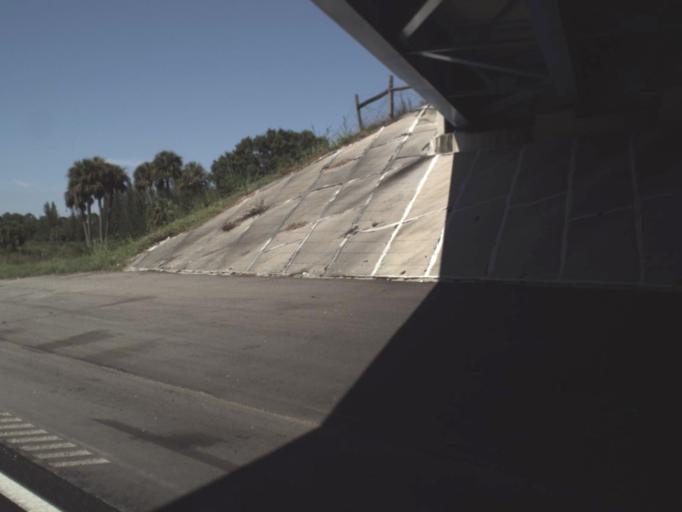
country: US
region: Florida
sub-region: Lee County
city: Suncoast Estates
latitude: 26.7399
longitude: -81.8506
